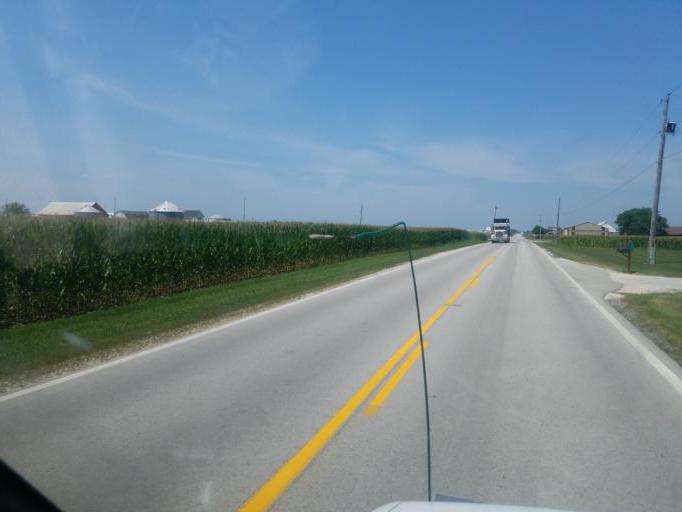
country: US
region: Ohio
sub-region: Auglaize County
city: New Bremen
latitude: 40.4348
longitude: -84.4338
